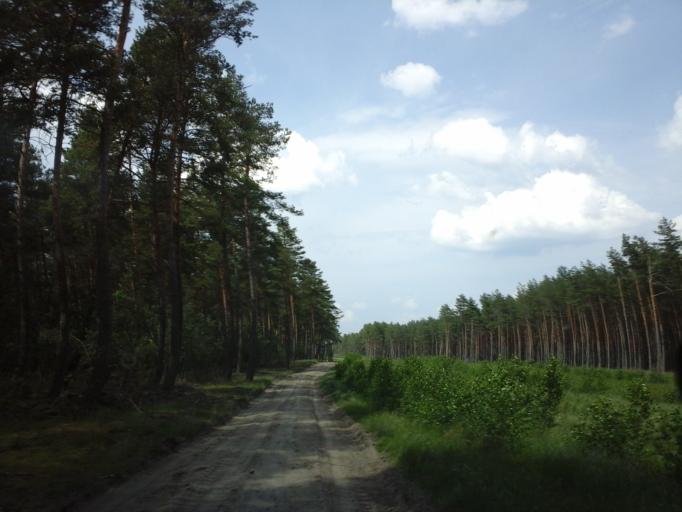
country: PL
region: West Pomeranian Voivodeship
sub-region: Powiat choszczenski
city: Drawno
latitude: 53.1674
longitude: 15.7535
